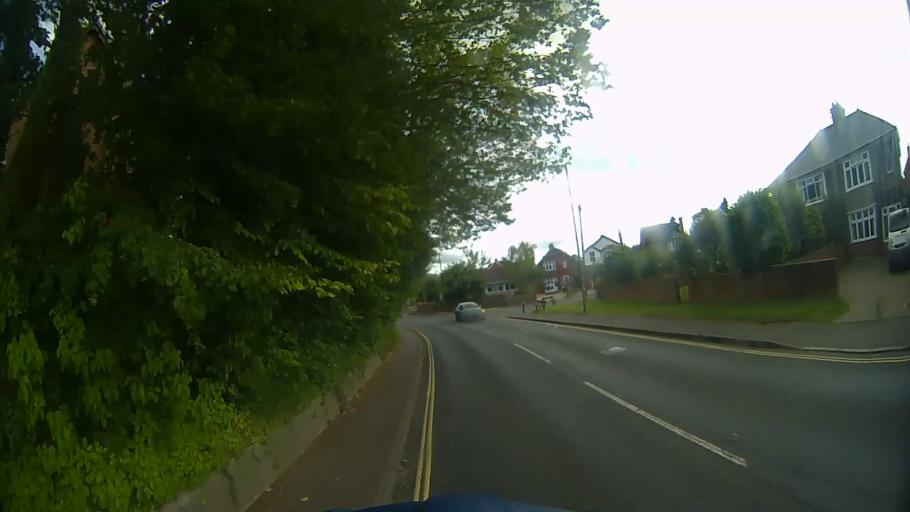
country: GB
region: England
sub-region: Hampshire
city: Andover
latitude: 51.2142
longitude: -1.4944
